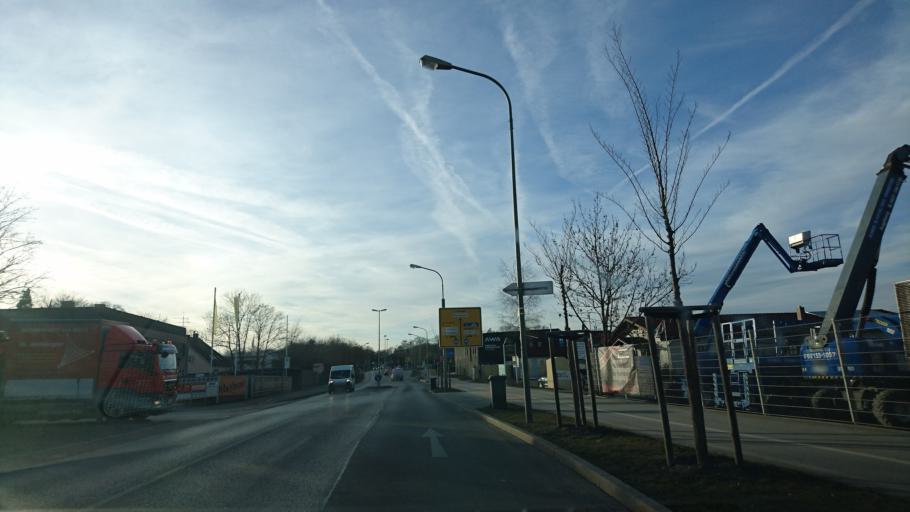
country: DE
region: Bavaria
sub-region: Swabia
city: Stadtbergen
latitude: 48.3902
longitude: 10.8652
